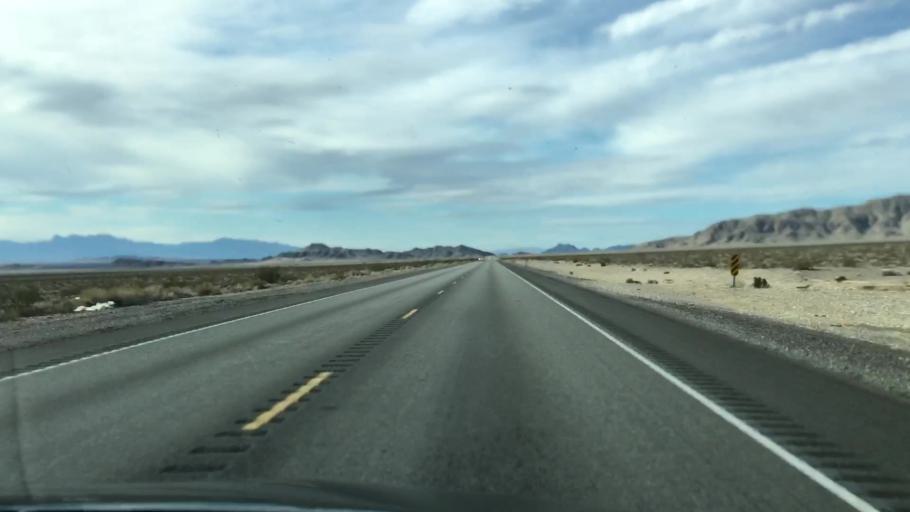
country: US
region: Nevada
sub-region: Nye County
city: Pahrump
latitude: 36.5678
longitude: -116.1477
